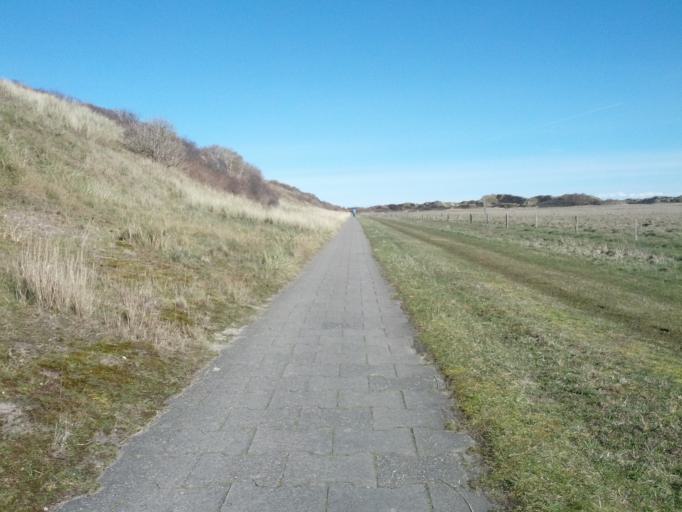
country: DE
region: Lower Saxony
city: Langeoog
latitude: 53.7543
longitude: 7.5236
